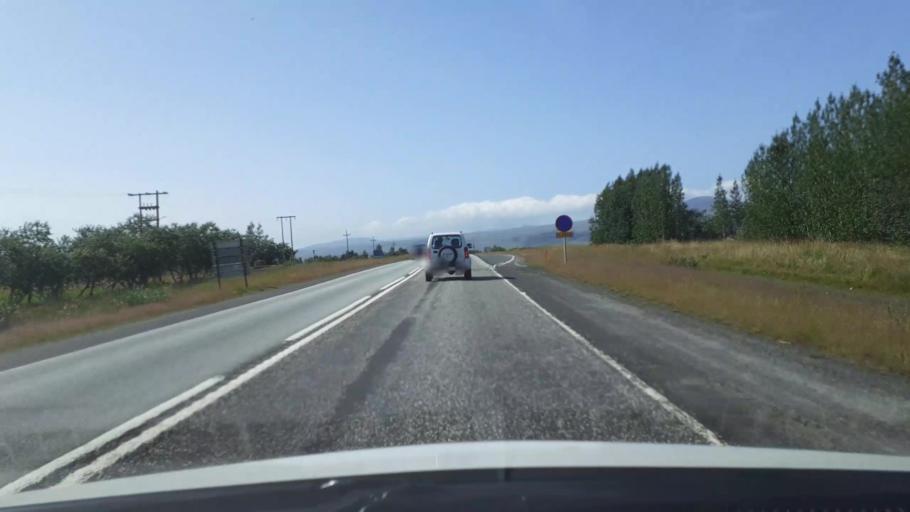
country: IS
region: South
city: Hveragerdi
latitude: 63.9587
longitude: -21.1021
